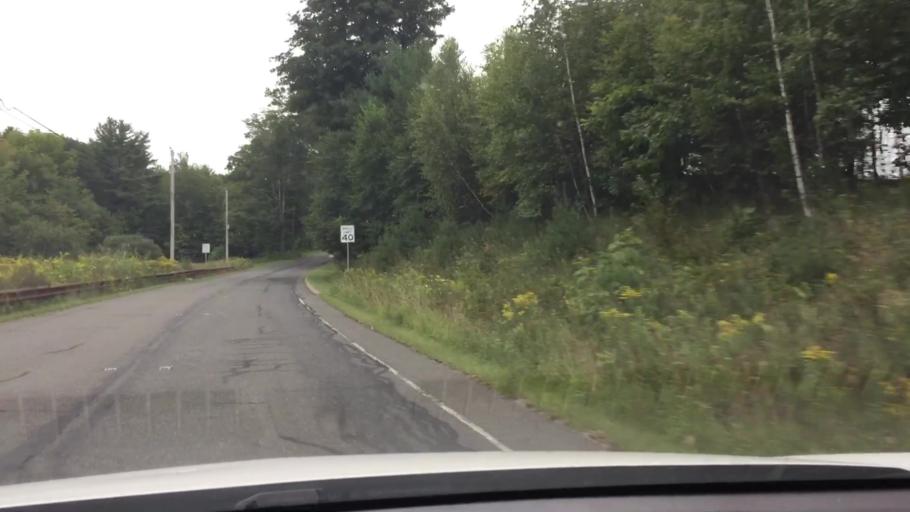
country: US
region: Massachusetts
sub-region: Berkshire County
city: Becket
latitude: 42.2596
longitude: -72.9991
